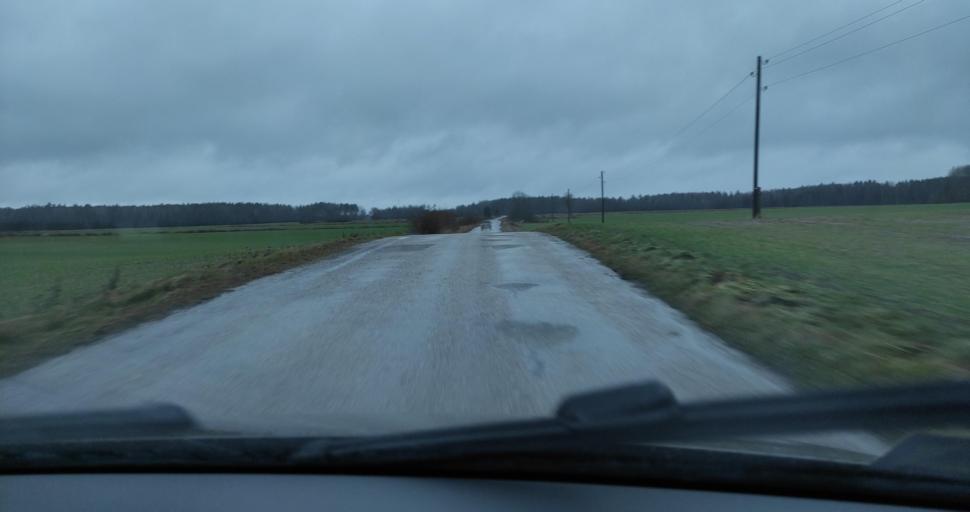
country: LV
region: Skrunda
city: Skrunda
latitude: 56.6456
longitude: 22.2296
